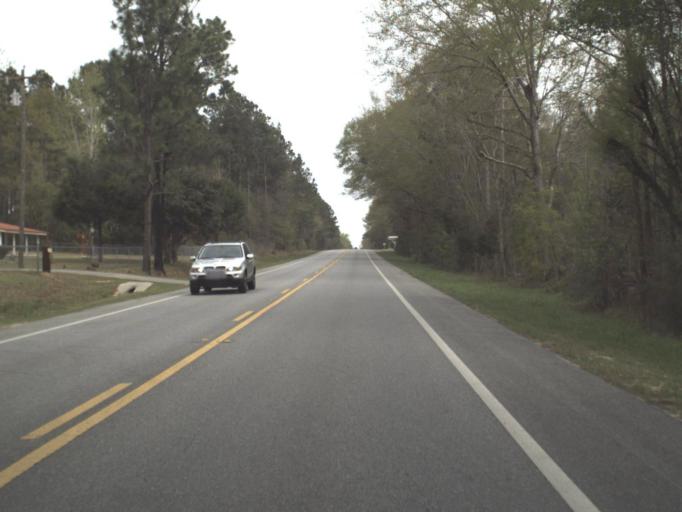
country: US
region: Florida
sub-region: Holmes County
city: Bonifay
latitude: 30.8485
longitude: -85.6667
